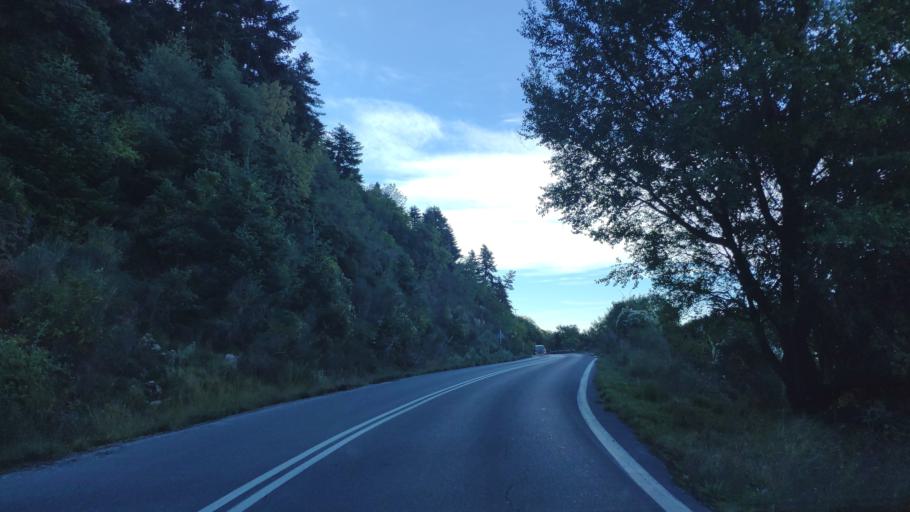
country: GR
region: Peloponnese
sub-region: Nomos Arkadias
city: Dimitsana
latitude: 37.5752
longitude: 22.0621
